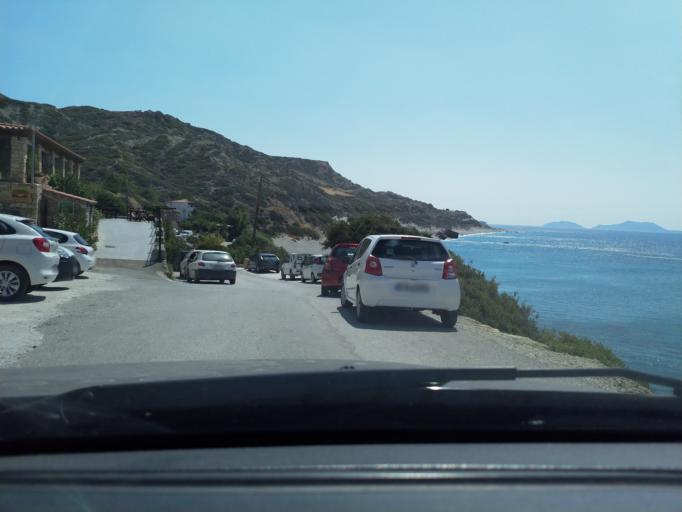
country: GR
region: Crete
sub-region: Nomos Rethymnis
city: Agia Foteini
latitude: 35.1386
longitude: 24.5284
